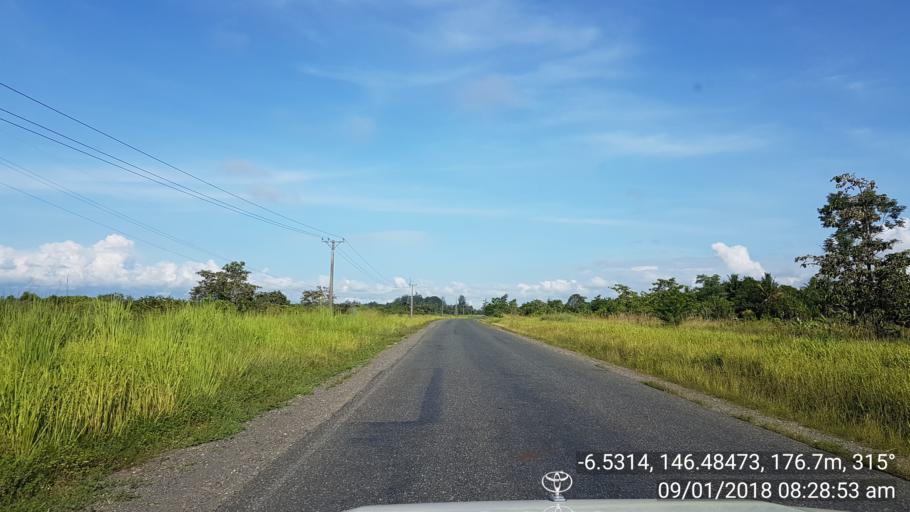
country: PG
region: Morobe
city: Lae
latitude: -6.5314
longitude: 146.4847
